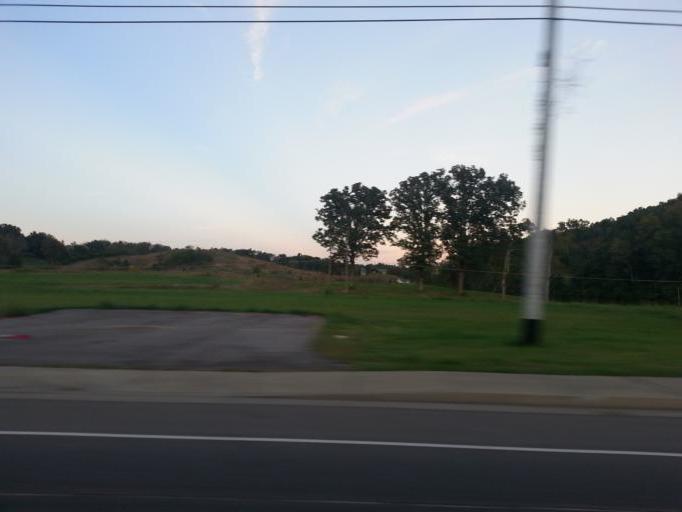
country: US
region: Tennessee
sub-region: Sevier County
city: Sevierville
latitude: 35.9252
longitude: -83.5821
